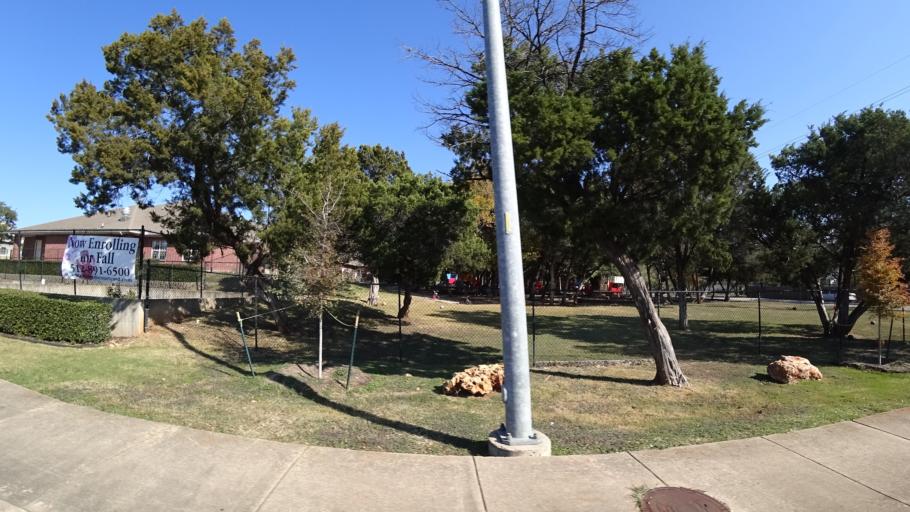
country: US
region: Texas
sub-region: Travis County
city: Barton Creek
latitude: 30.2284
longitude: -97.8616
